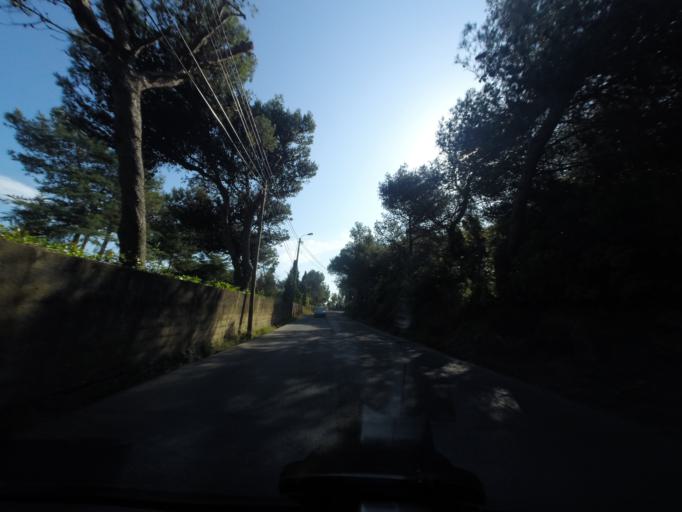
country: PT
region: Lisbon
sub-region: Cascais
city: Alcabideche
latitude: 38.7346
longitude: -9.4160
